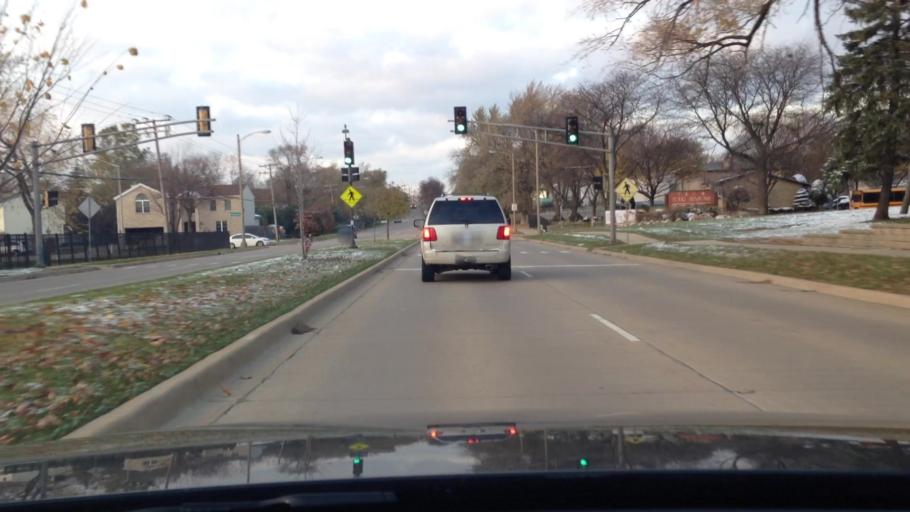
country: US
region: Illinois
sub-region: DuPage County
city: Lombard
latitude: 41.8516
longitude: -88.0266
